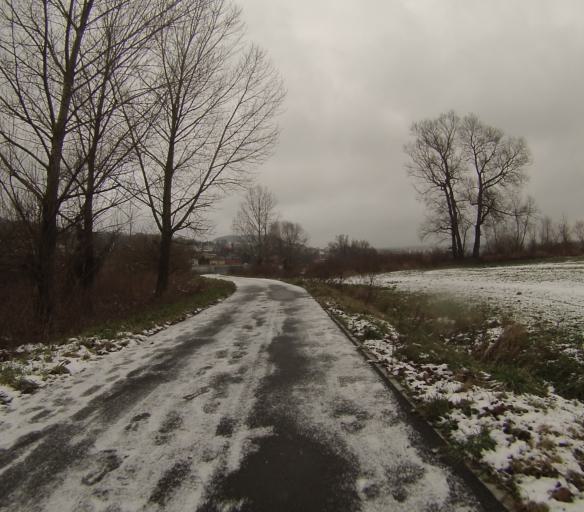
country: CZ
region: Ustecky
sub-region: Okres Decin
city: Decin
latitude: 50.7461
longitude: 14.1840
